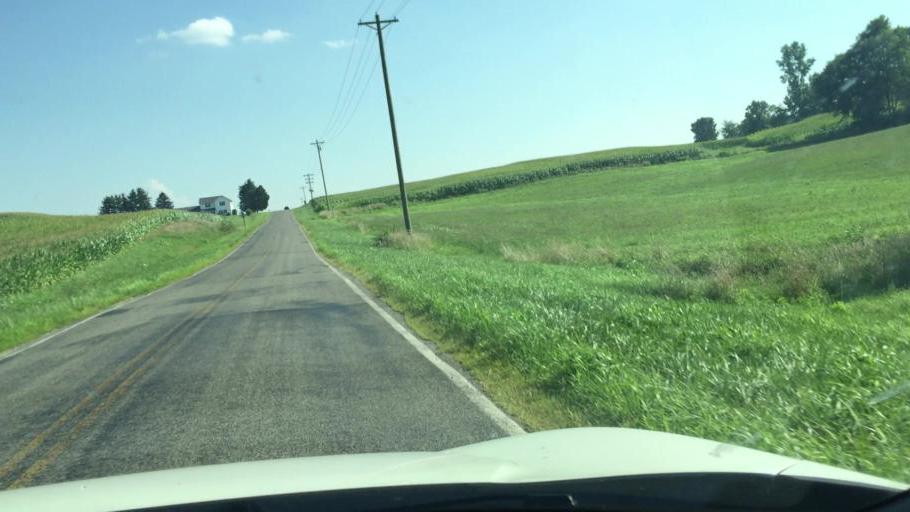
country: US
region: Ohio
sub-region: Champaign County
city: Mechanicsburg
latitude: 40.0535
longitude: -83.6561
